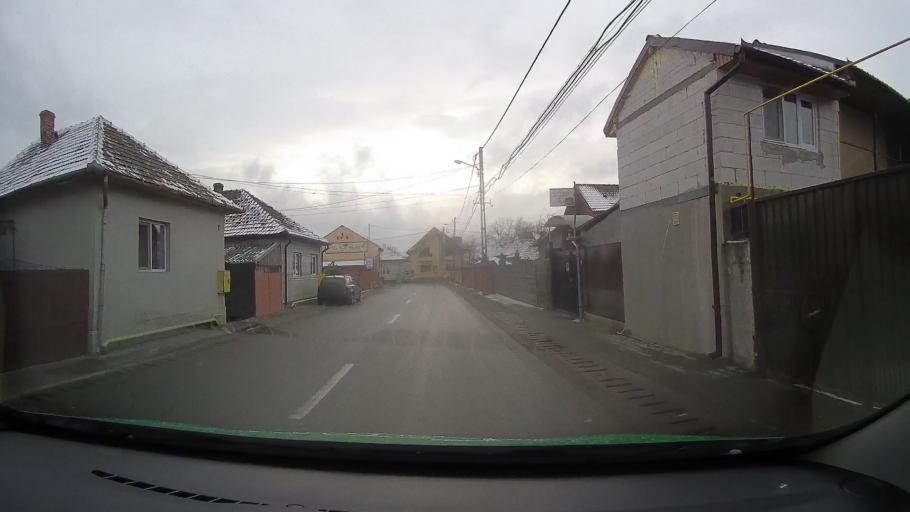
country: RO
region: Hunedoara
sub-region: Oras Hateg
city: Hateg
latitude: 45.6136
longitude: 22.9449
